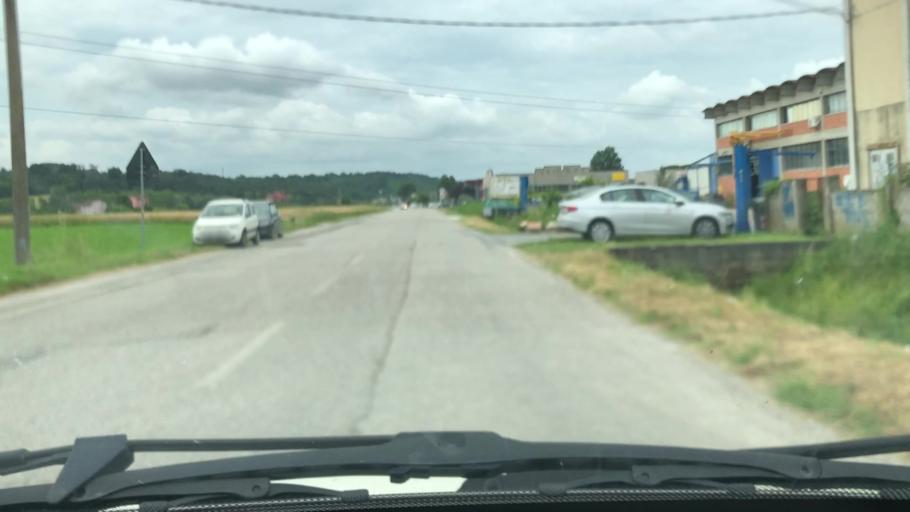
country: IT
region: Tuscany
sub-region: Province of Pisa
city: Bientina
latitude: 43.6987
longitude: 10.6242
